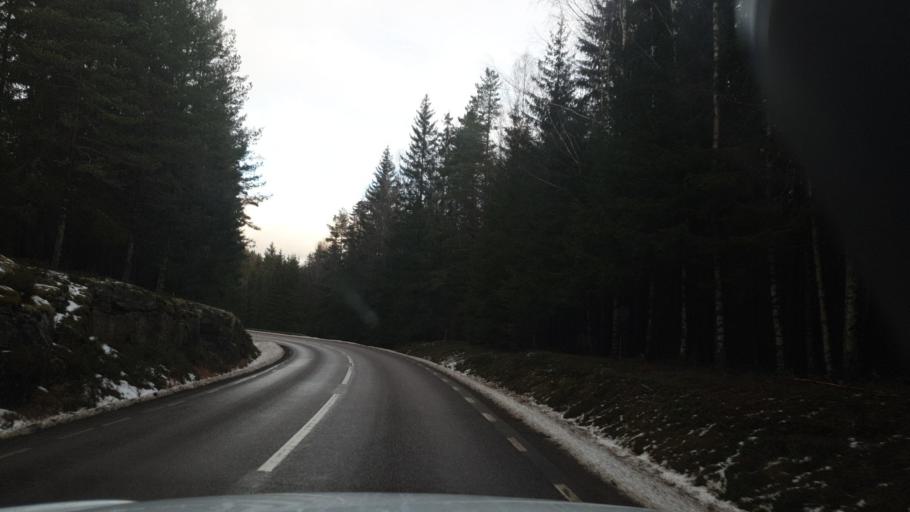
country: SE
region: Vaermland
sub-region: Eda Kommun
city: Amotfors
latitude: 59.6592
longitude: 12.3772
